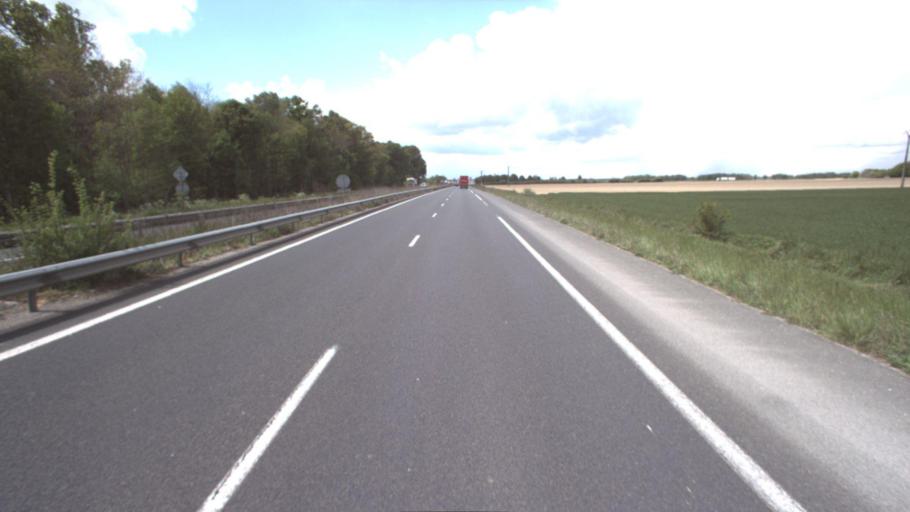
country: FR
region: Ile-de-France
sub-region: Departement de Seine-et-Marne
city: Fontenay-Tresigny
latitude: 48.6943
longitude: 2.9089
